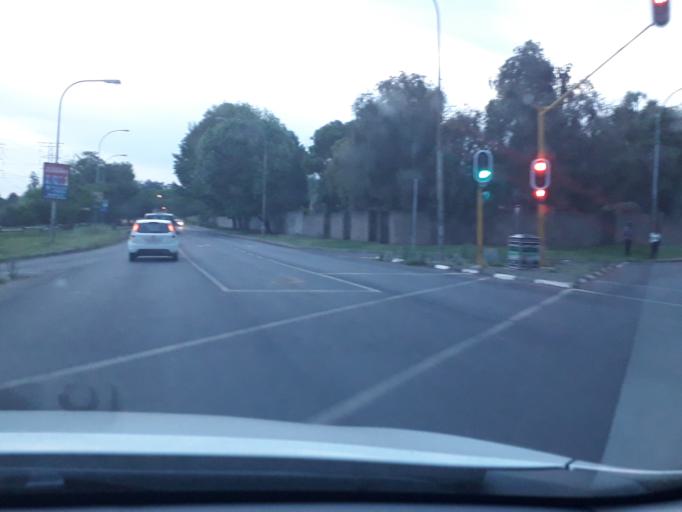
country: ZA
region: Gauteng
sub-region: City of Johannesburg Metropolitan Municipality
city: Johannesburg
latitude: -26.1446
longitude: 28.0036
